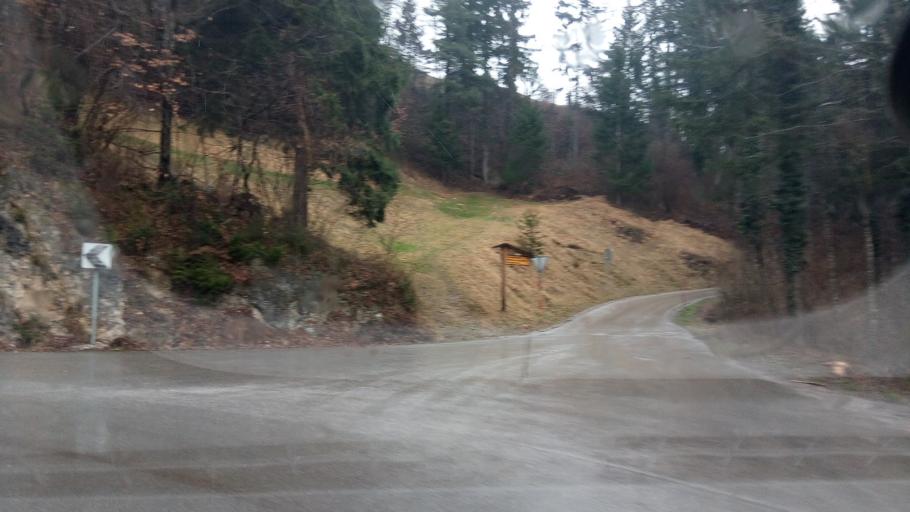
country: SI
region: Horjul
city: Horjul
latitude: 46.0076
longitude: 14.2250
